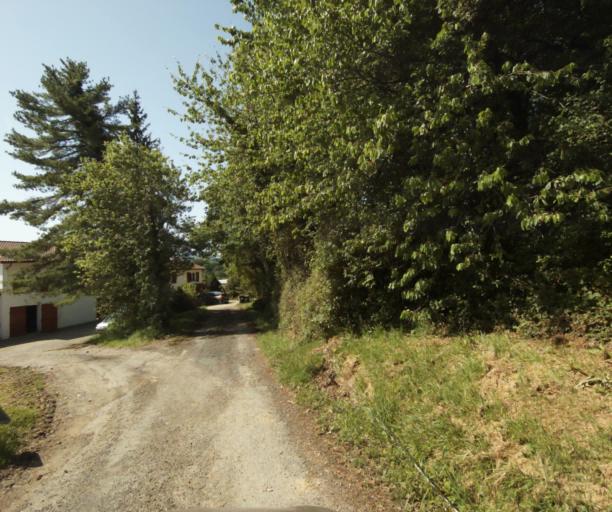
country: FR
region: Aquitaine
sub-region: Departement des Pyrenees-Atlantiques
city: Villefranque
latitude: 43.4523
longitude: -1.4390
